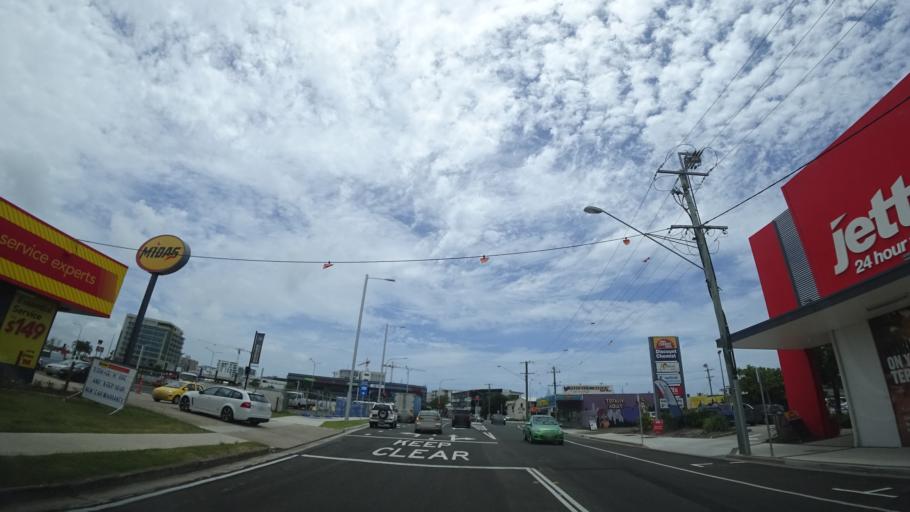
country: AU
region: Queensland
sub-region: Sunshine Coast
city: Mooloolaba
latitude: -26.6580
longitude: 153.0937
